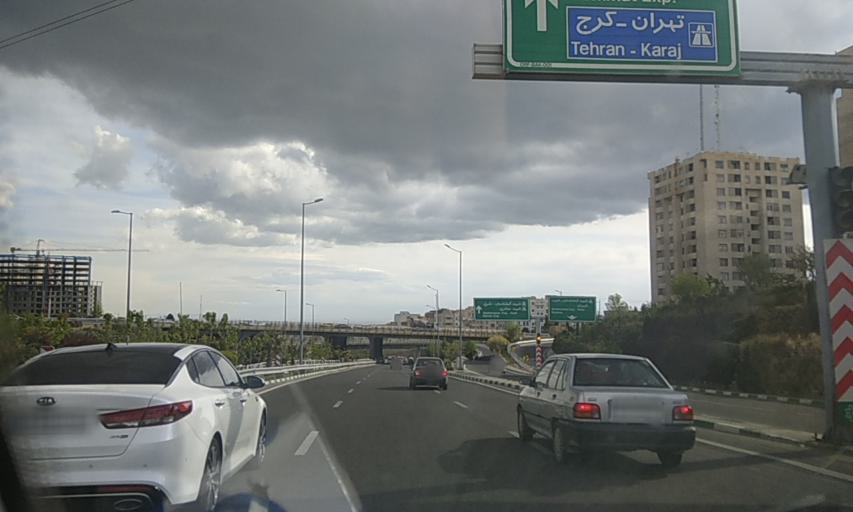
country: IR
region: Tehran
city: Tajrish
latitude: 35.7653
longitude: 51.2976
